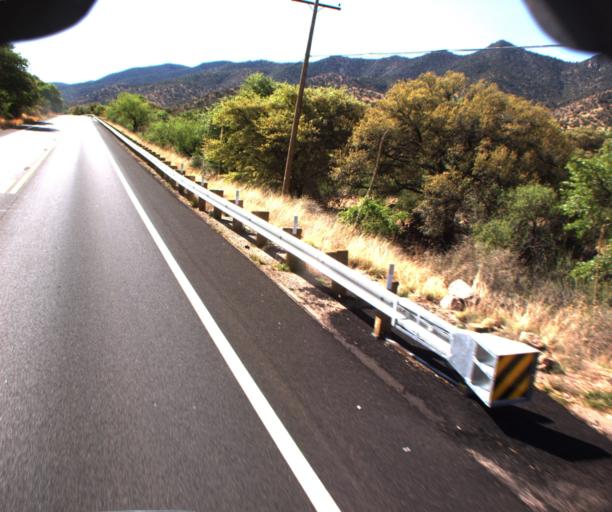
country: US
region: Arizona
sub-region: Cochise County
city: Bisbee
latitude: 31.4866
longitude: -109.9862
